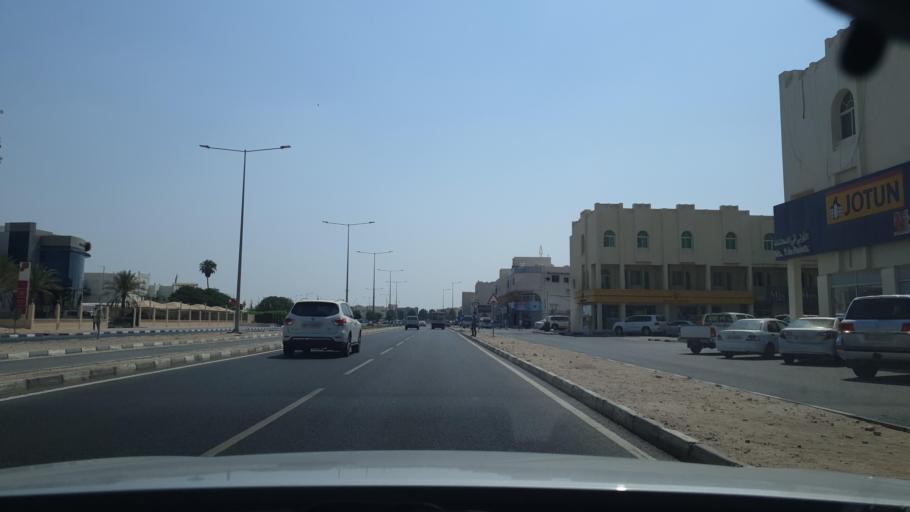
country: QA
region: Al Khawr
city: Al Khawr
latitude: 25.6839
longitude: 51.4956
